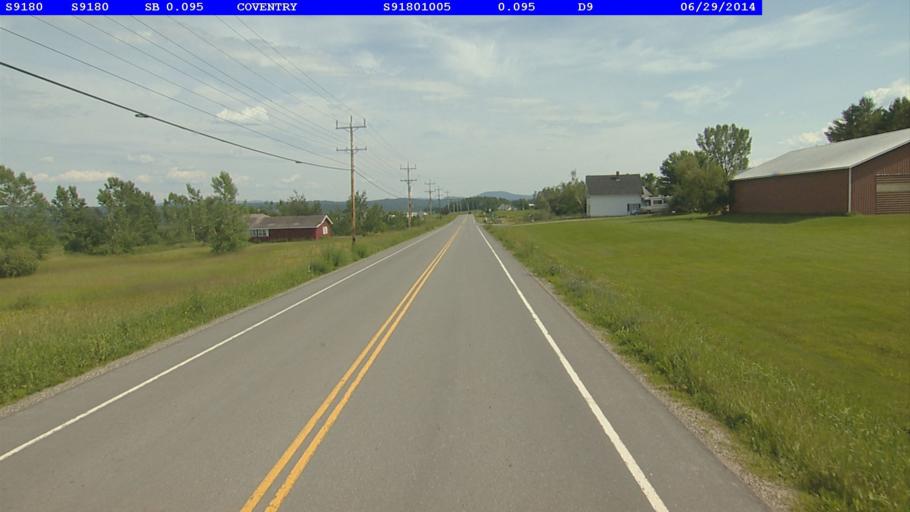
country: US
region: Vermont
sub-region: Orleans County
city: Newport
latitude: 44.8903
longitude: -72.2240
